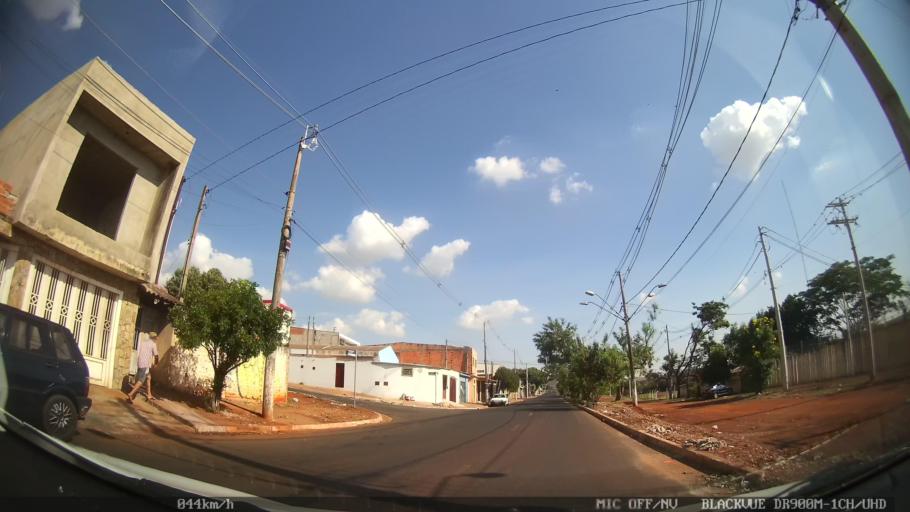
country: BR
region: Sao Paulo
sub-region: Ribeirao Preto
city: Ribeirao Preto
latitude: -21.1982
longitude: -47.8539
